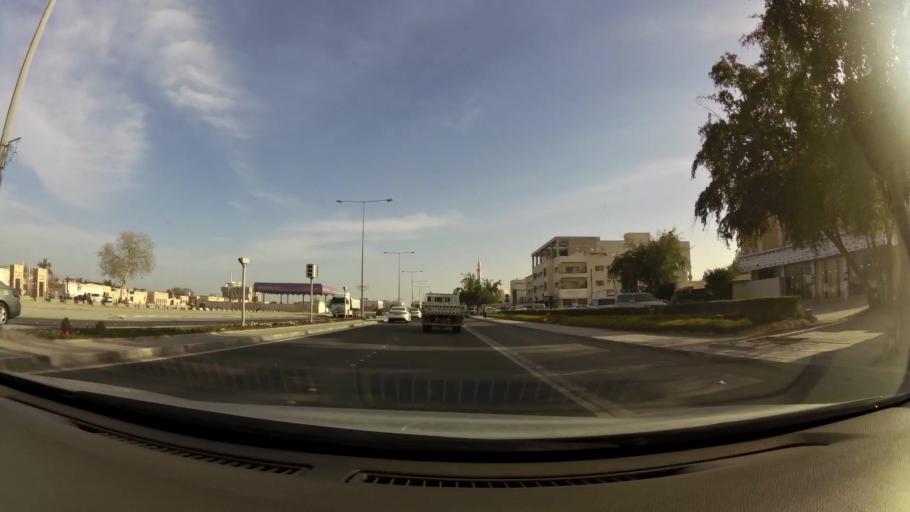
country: QA
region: Al Wakrah
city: Al Wakrah
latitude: 25.1703
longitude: 51.6073
